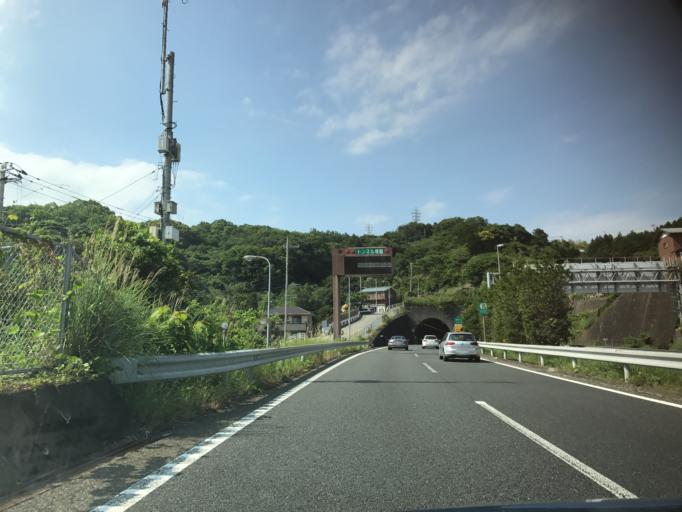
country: JP
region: Kanagawa
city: Odawara
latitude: 35.2477
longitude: 139.1325
